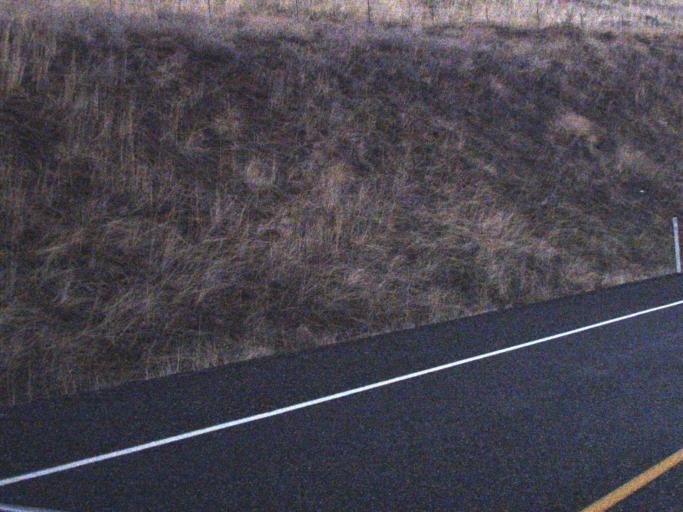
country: US
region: Washington
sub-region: Garfield County
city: Pomeroy
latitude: 46.5977
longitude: -117.7845
